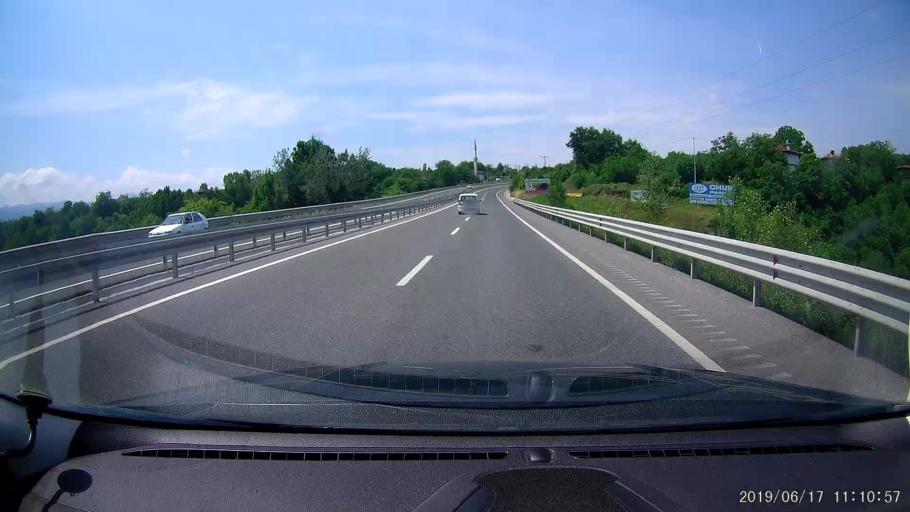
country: TR
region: Kastamonu
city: Tosya
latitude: 40.9931
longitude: 34.0161
